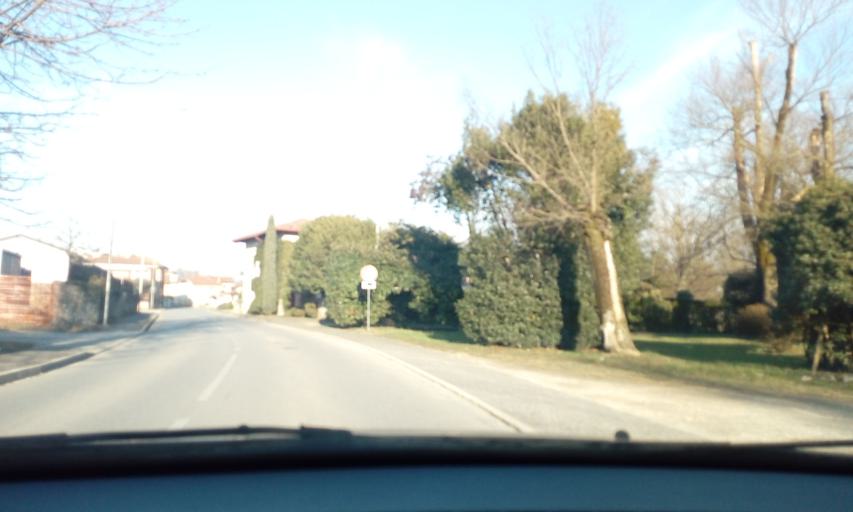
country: IT
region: Friuli Venezia Giulia
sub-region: Provincia di Udine
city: San Giovanni al Natisone
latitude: 45.9563
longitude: 13.4203
